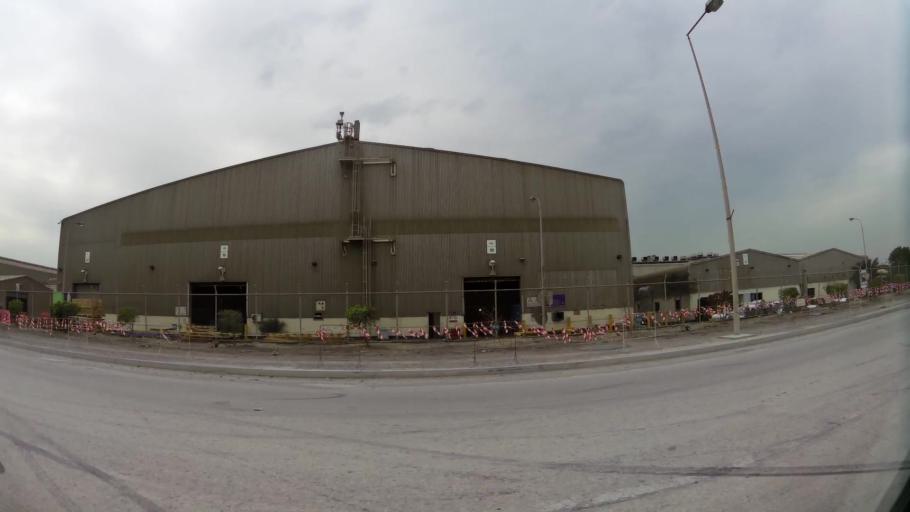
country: BH
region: Northern
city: Sitrah
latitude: 26.1823
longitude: 50.6154
